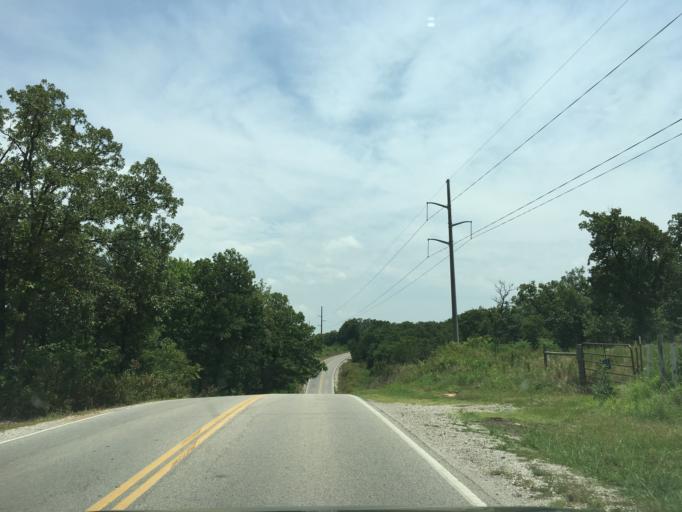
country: US
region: Oklahoma
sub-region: Tulsa County
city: Oakhurst
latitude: 36.0752
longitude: -96.0030
